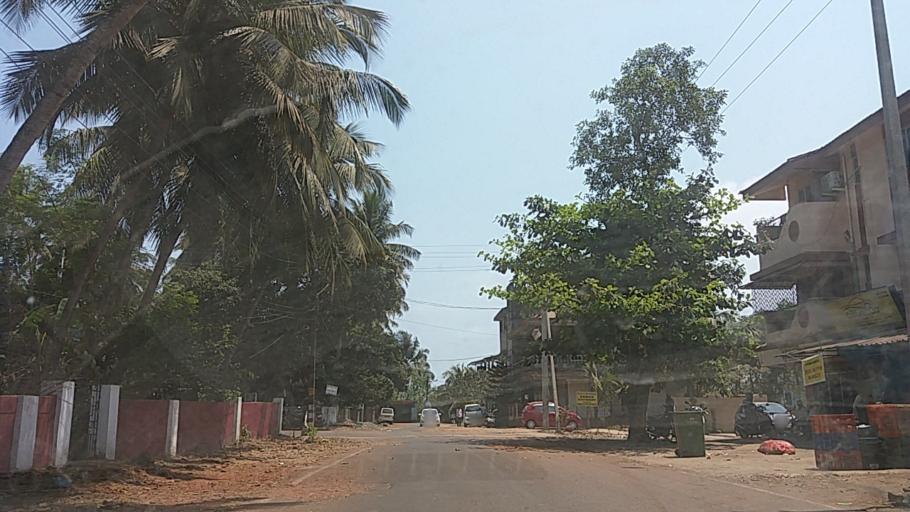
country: IN
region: Goa
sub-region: North Goa
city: Serula
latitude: 15.5235
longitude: 73.8343
